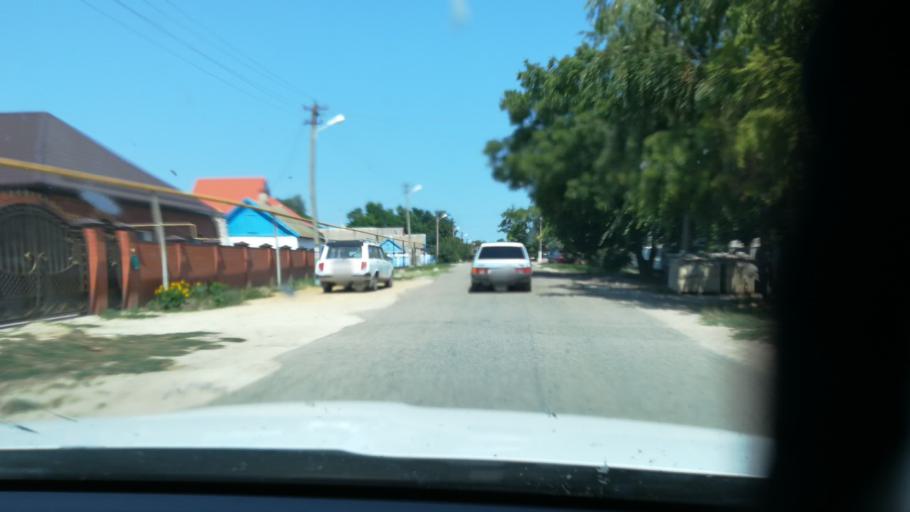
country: RU
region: Krasnodarskiy
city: Starotitarovskaya
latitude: 45.2145
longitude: 37.1434
